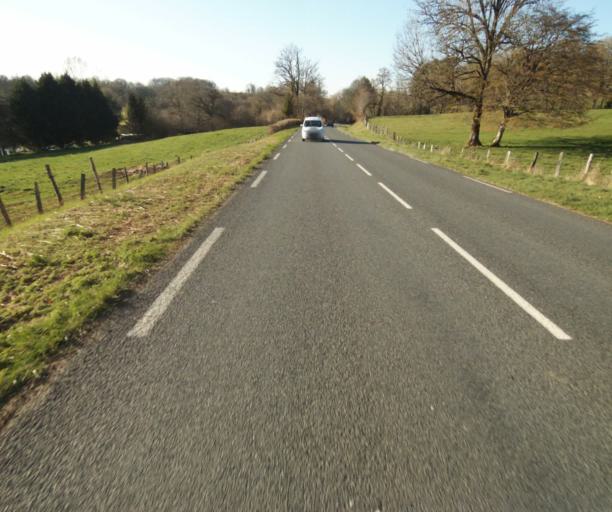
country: FR
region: Limousin
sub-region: Departement de la Correze
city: Seilhac
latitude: 45.3923
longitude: 1.7187
